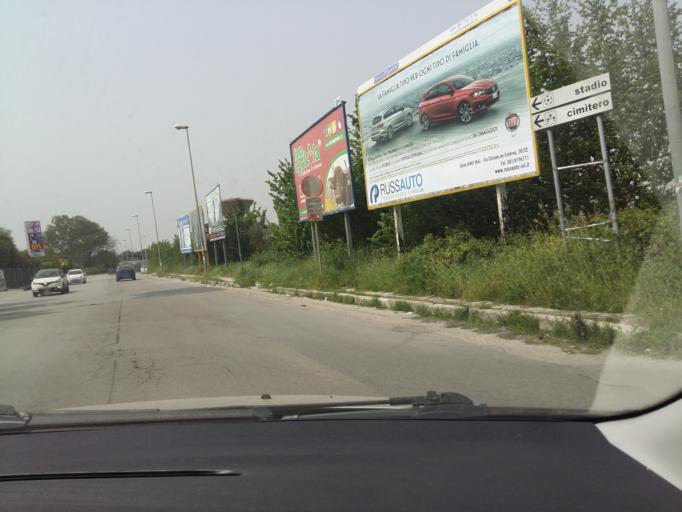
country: IT
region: Campania
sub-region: Provincia di Napoli
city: Mugnano di Napoli
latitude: 40.8995
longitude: 14.2057
